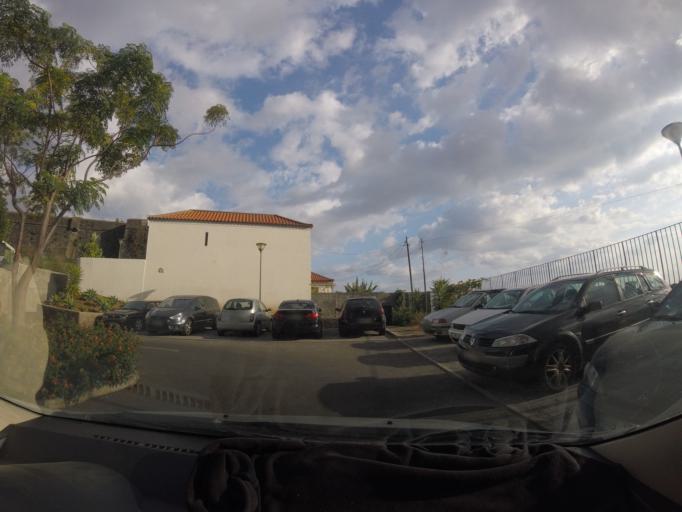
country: PT
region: Madeira
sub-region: Funchal
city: Nossa Senhora do Monte
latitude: 32.6511
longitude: -16.9173
